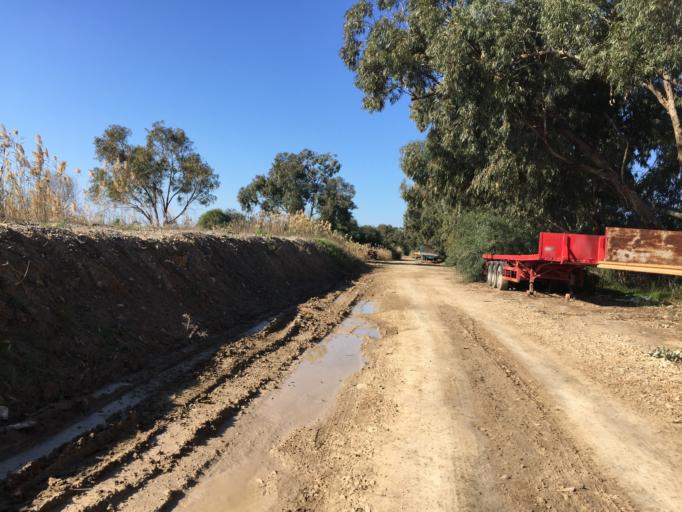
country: CY
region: Limassol
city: Limassol
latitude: 34.6439
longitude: 33.0009
